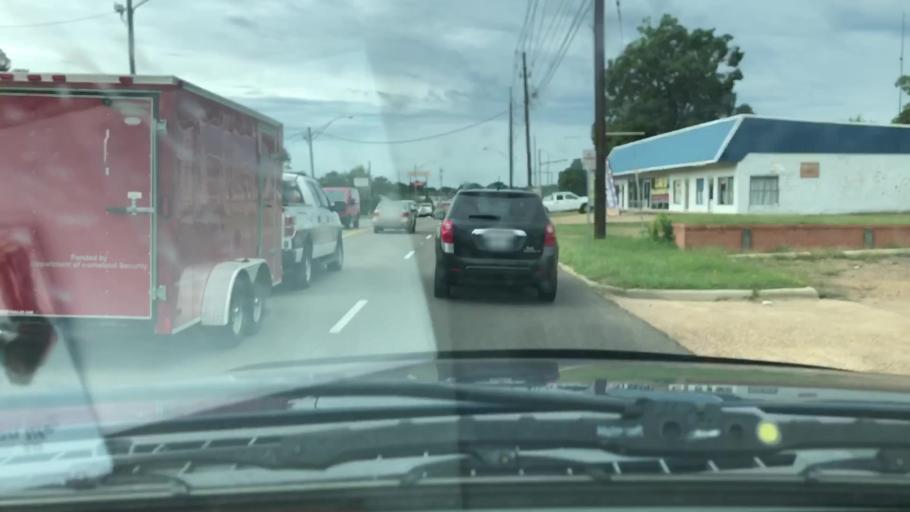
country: US
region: Texas
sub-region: Bowie County
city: Texarkana
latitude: 33.4350
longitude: -94.0705
